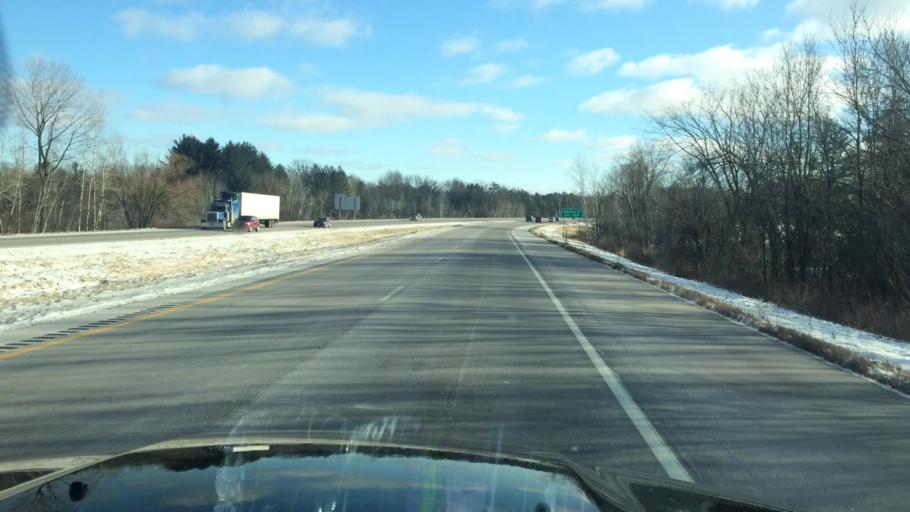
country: US
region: Wisconsin
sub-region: Portage County
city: Stevens Point
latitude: 44.5482
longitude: -89.5591
